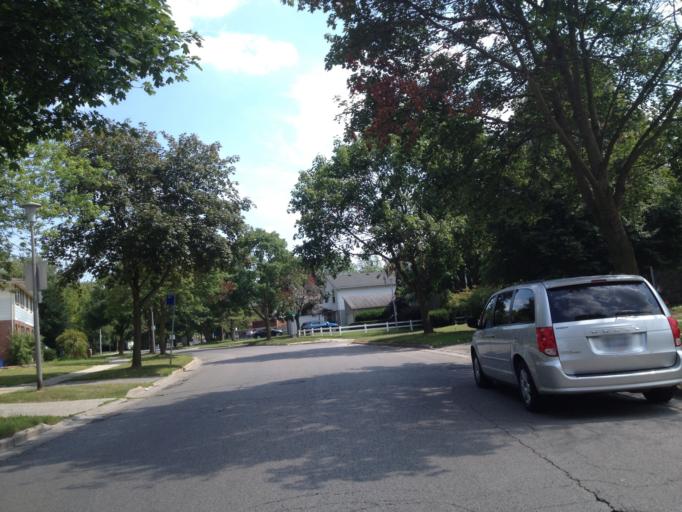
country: CA
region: Ontario
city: London
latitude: 43.0052
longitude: -81.3176
